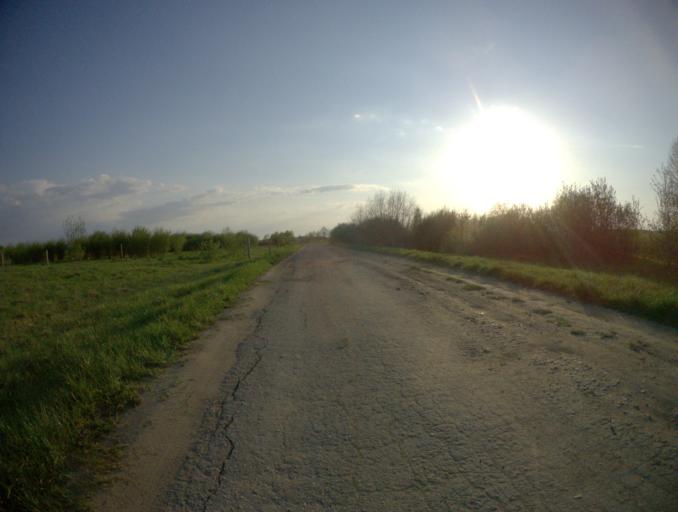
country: RU
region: Vladimir
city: Vyazniki
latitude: 56.3208
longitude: 42.1143
